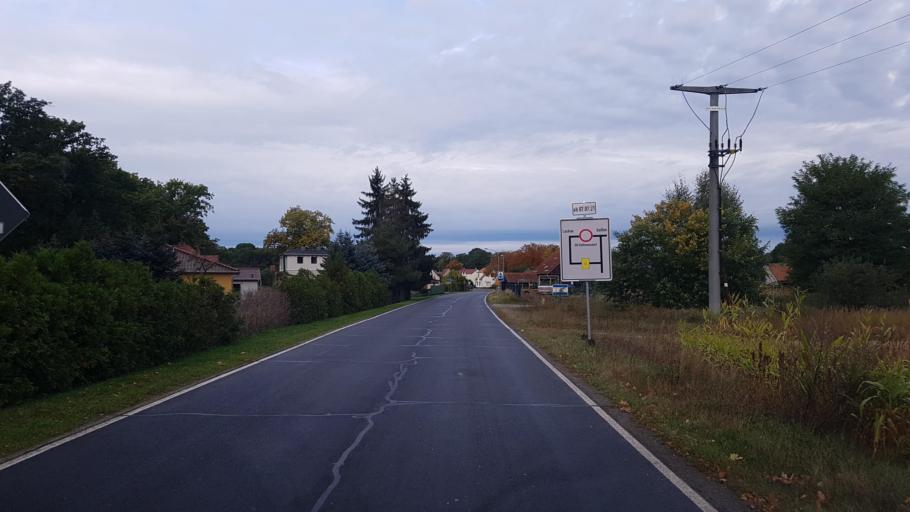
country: DE
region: Brandenburg
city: Kasel-Golzig
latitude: 51.9348
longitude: 13.7082
